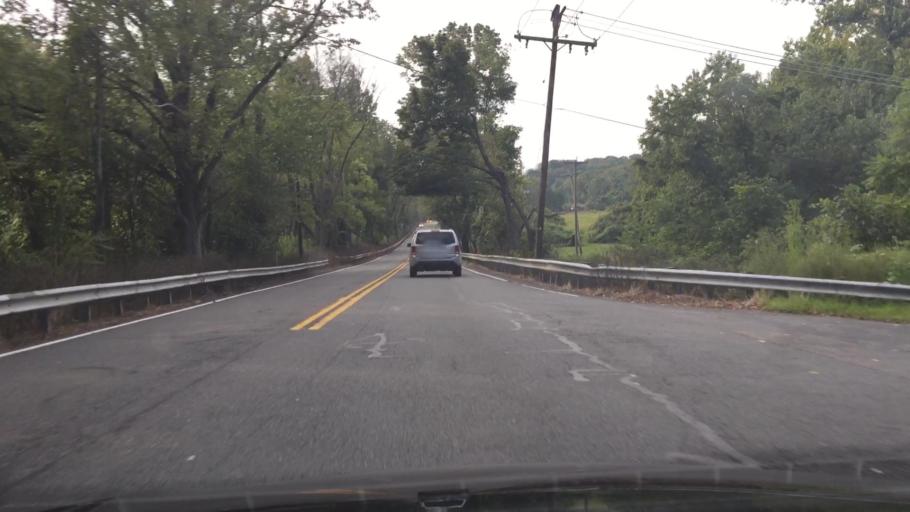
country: US
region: New Jersey
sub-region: Hunterdon County
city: Lambertville
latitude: 40.3239
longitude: -74.9167
